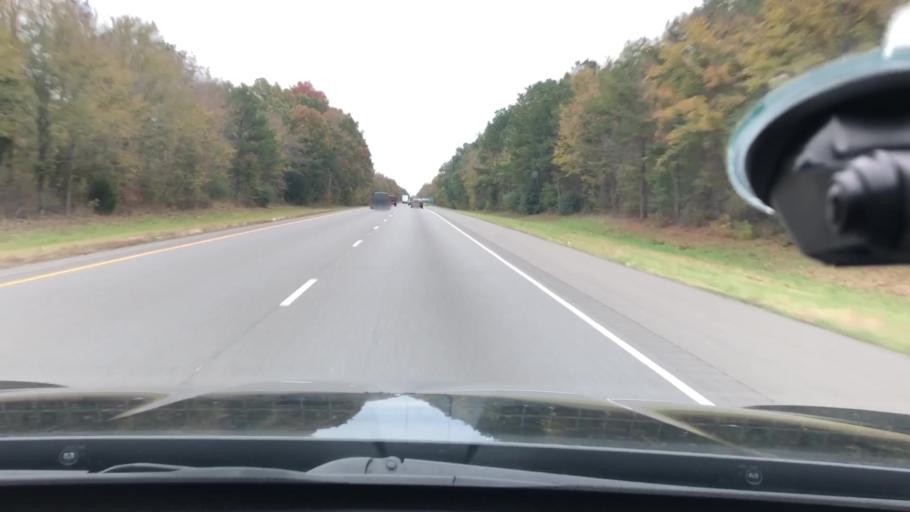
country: US
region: Arkansas
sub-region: Hempstead County
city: Hope
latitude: 33.6412
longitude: -93.6953
